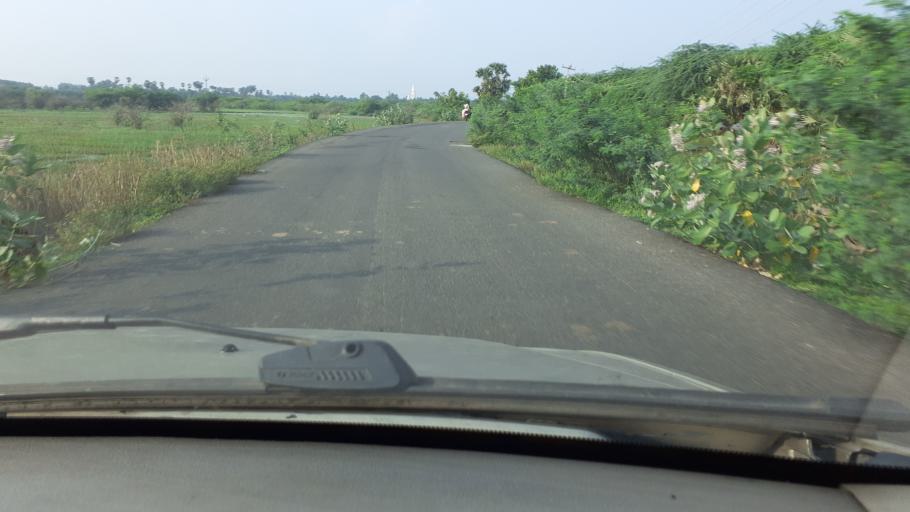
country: IN
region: Tamil Nadu
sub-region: Thoothukkudi
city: Alwar Tirunagari
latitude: 8.5827
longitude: 77.9789
